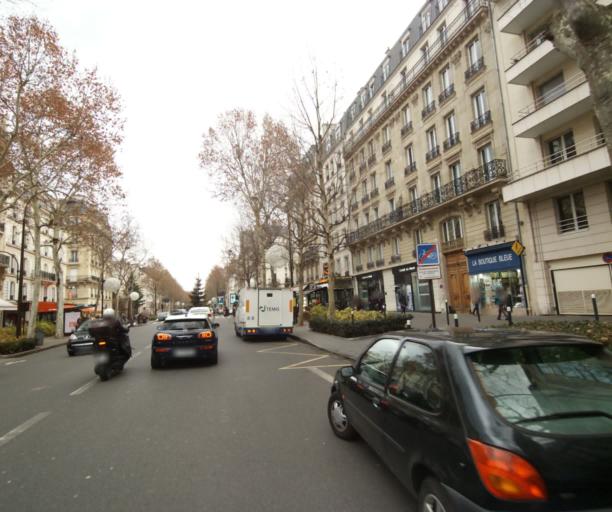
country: FR
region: Ile-de-France
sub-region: Departement des Hauts-de-Seine
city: Neuilly-sur-Seine
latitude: 48.8827
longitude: 2.2763
